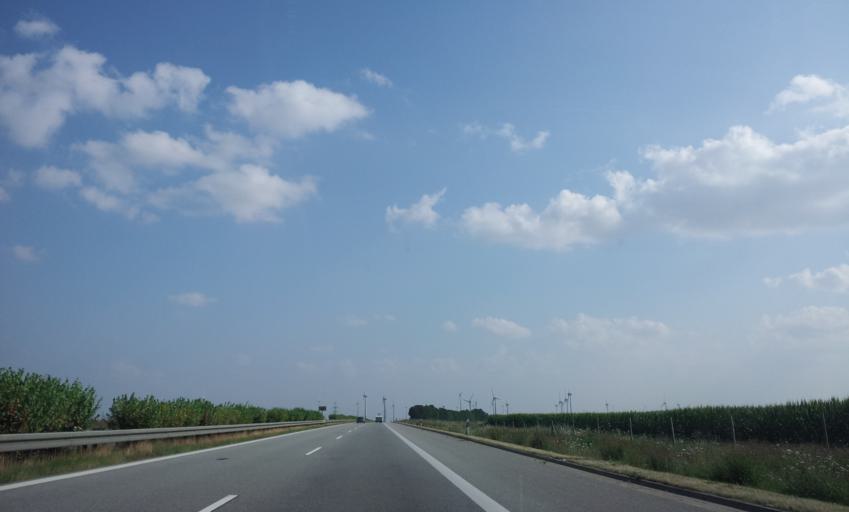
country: DE
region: Mecklenburg-Vorpommern
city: Kessin
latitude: 53.7648
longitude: 13.3316
